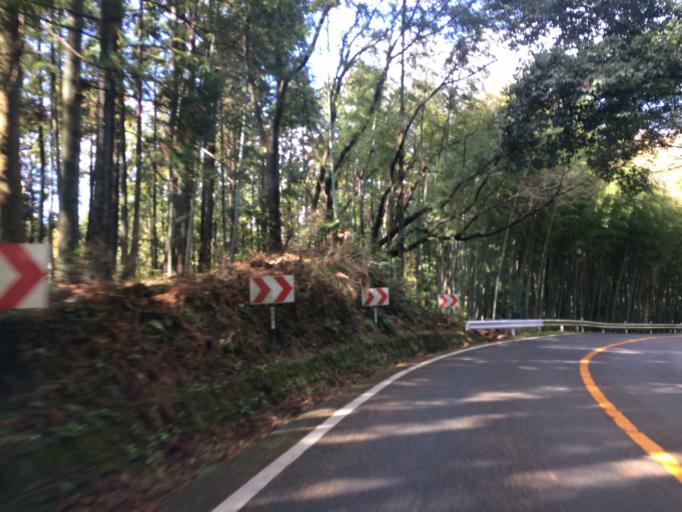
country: JP
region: Shizuoka
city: Shizuoka-shi
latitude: 34.9813
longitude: 138.4447
